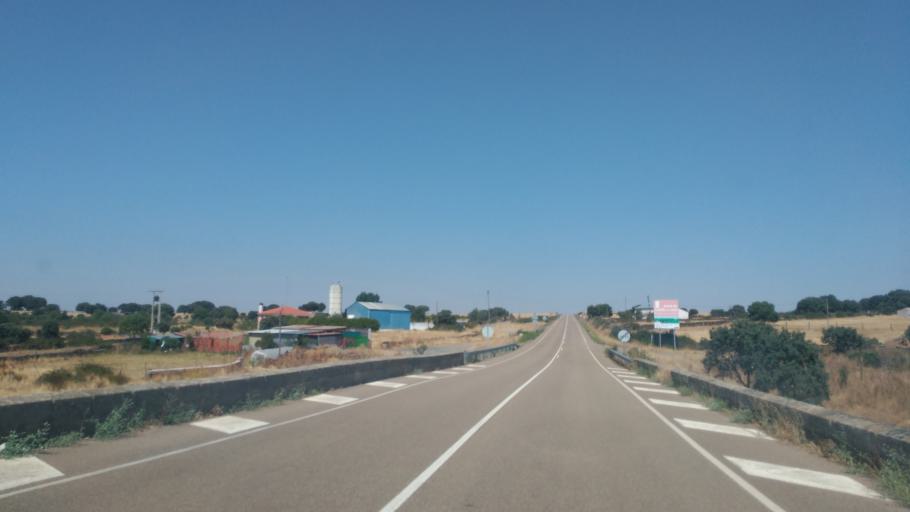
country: ES
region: Castille and Leon
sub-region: Provincia de Salamanca
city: Aldeanueva de la Sierra
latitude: 40.6169
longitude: -6.1005
